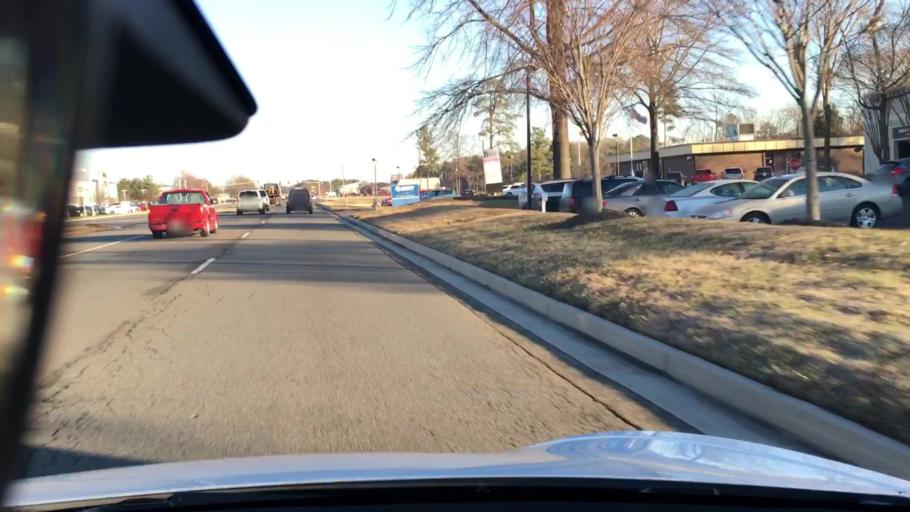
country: US
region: Virginia
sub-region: Henrico County
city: Fort Lee
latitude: 37.5084
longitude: -77.3494
